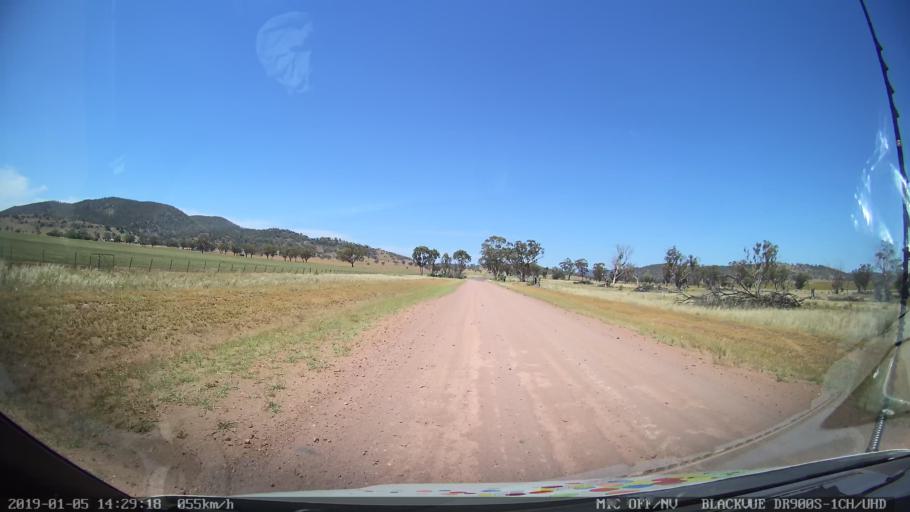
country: AU
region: New South Wales
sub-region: Tamworth Municipality
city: Phillip
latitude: -31.2294
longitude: 150.5806
